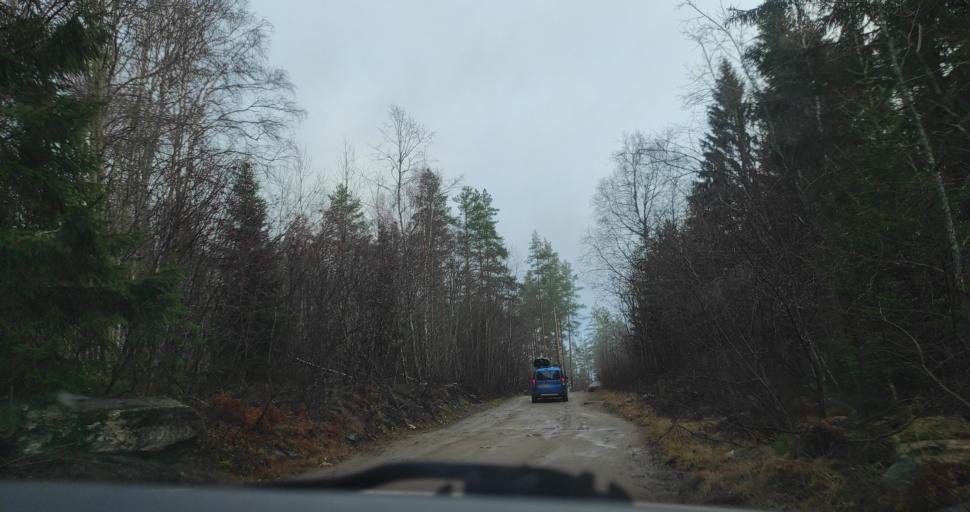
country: RU
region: Republic of Karelia
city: Pitkyaranta
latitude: 61.7385
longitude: 31.3895
